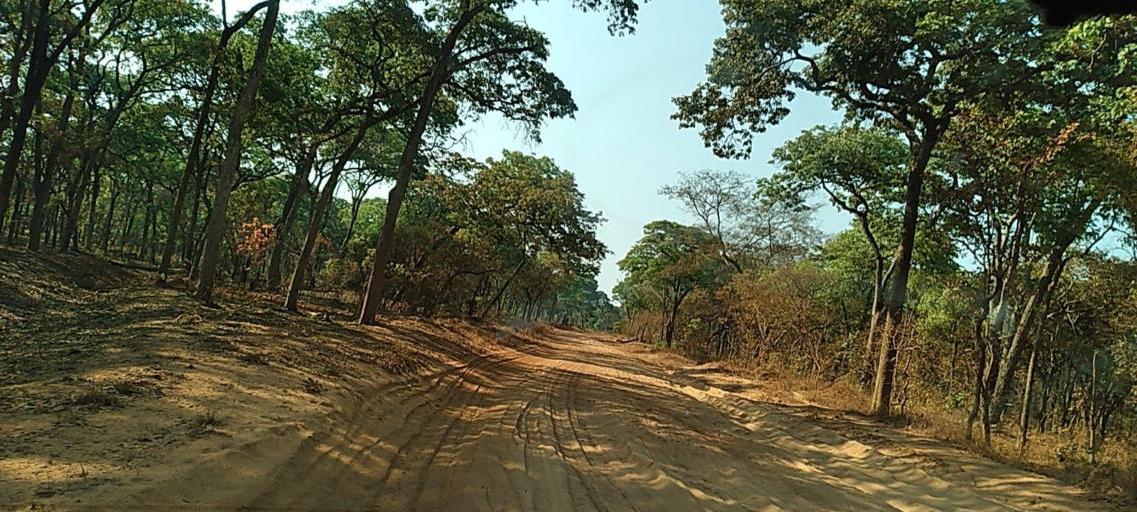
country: ZM
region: North-Western
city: Kasempa
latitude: -13.6554
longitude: 26.0076
